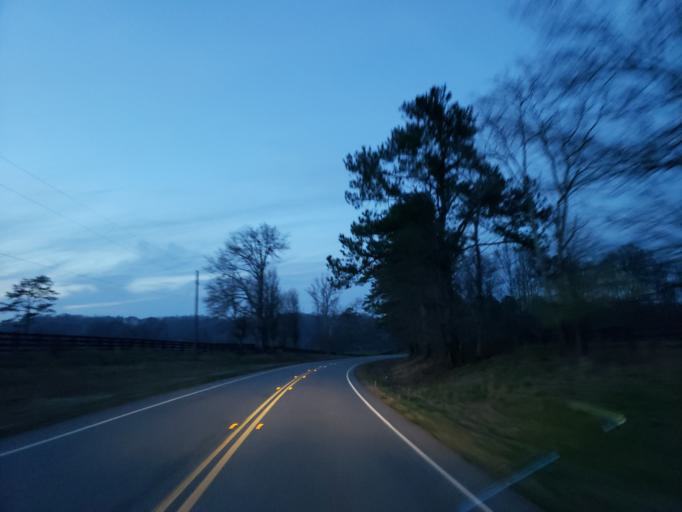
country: US
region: Georgia
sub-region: Cherokee County
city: Ball Ground
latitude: 34.2965
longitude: -84.2756
